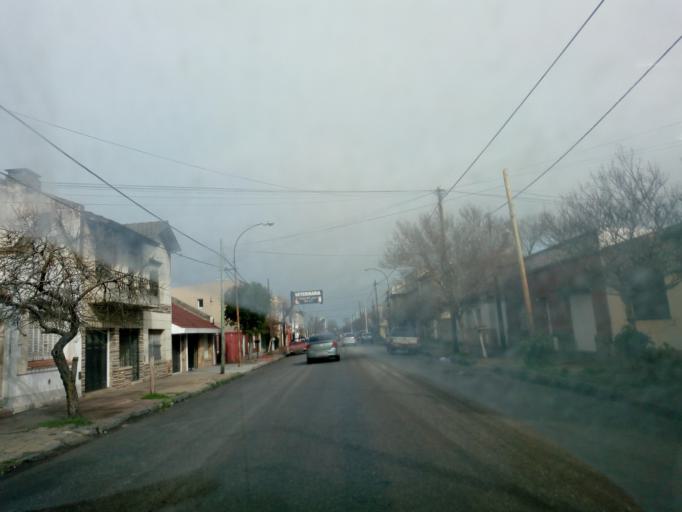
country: AR
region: Buenos Aires
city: Necochea
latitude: -38.5575
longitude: -58.7313
